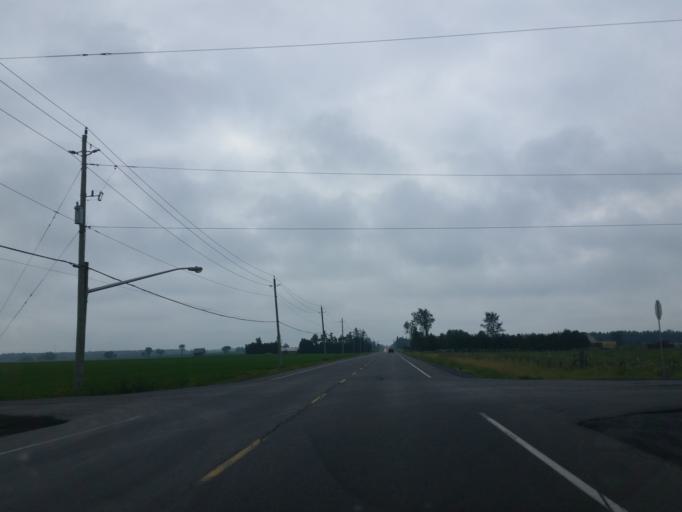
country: CA
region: Ontario
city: Clarence-Rockland
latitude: 45.4473
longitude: -75.4413
